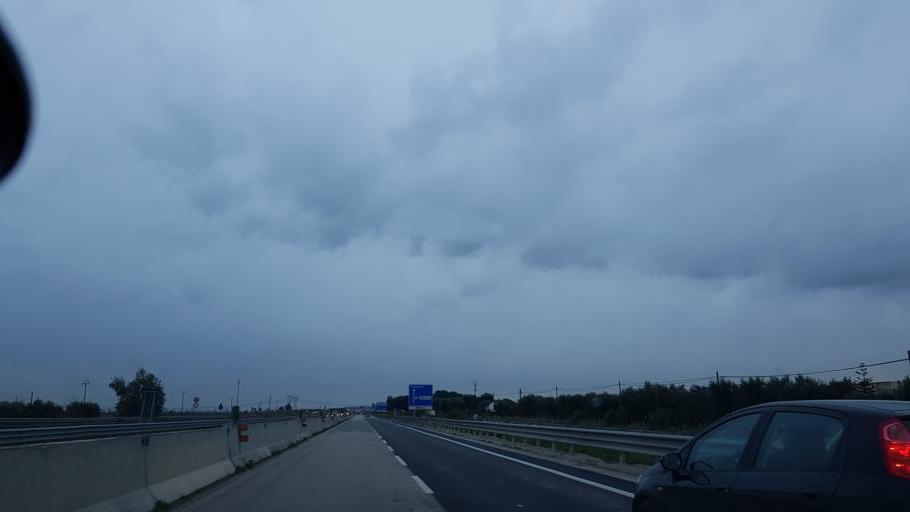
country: IT
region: Apulia
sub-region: Provincia di Brindisi
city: Brindisi
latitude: 40.6093
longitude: 17.8912
